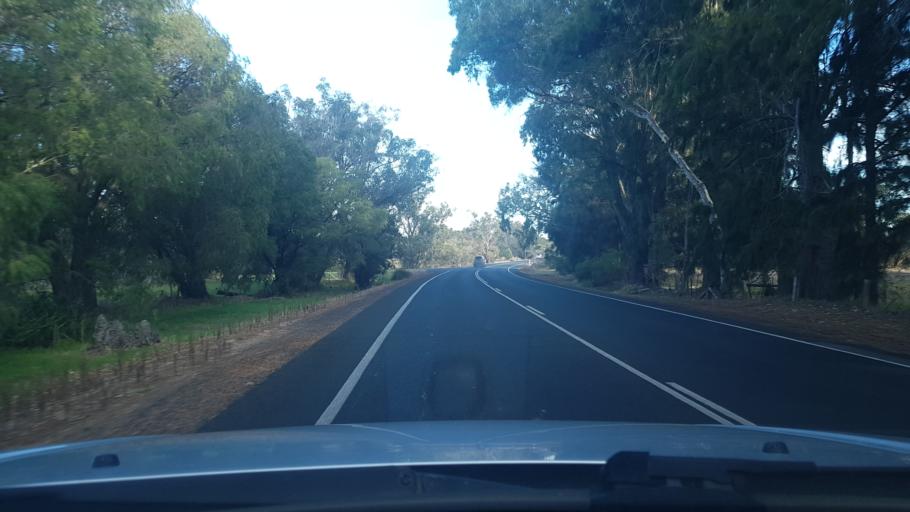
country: AU
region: Western Australia
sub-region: Busselton
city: Vasse
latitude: -33.6653
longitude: 115.2587
